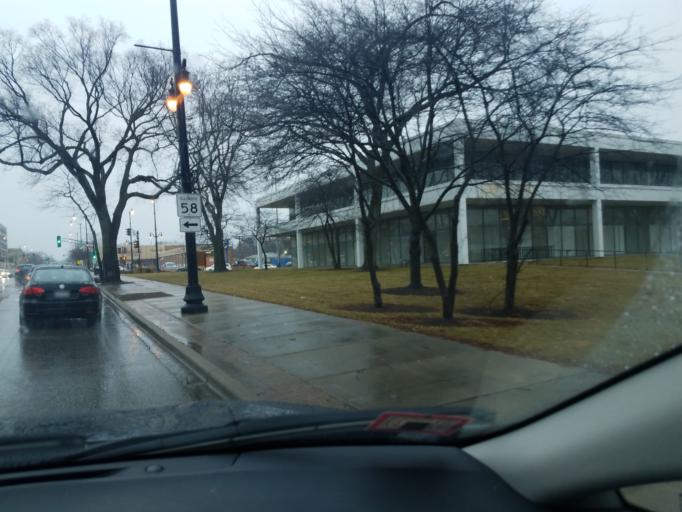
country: US
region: Illinois
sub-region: Cook County
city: Skokie
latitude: 42.0399
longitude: -87.7470
